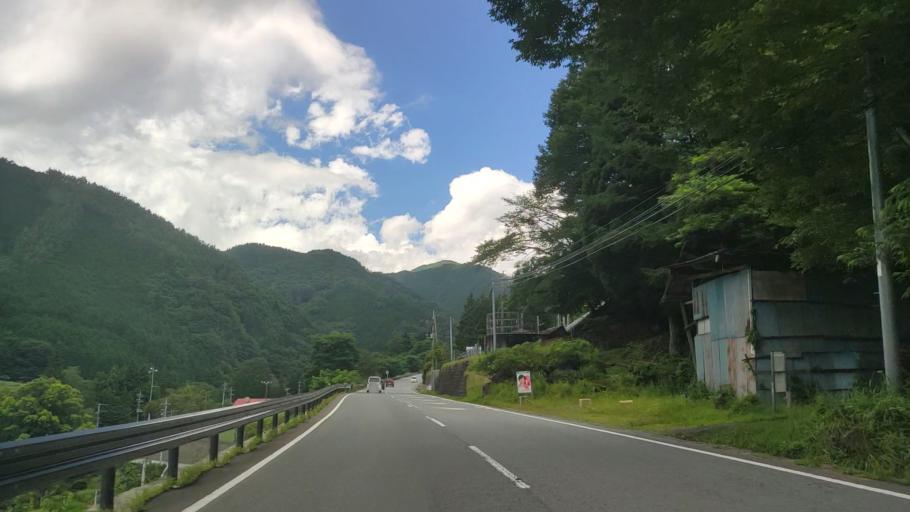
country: JP
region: Yamanashi
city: Enzan
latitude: 35.8080
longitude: 138.7514
